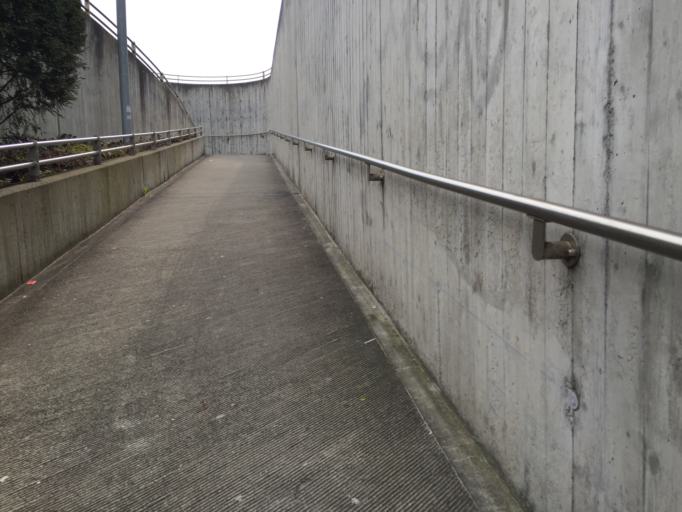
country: CH
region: Aargau
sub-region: Bezirk Zofingen
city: Zofingen
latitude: 47.2860
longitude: 7.9443
